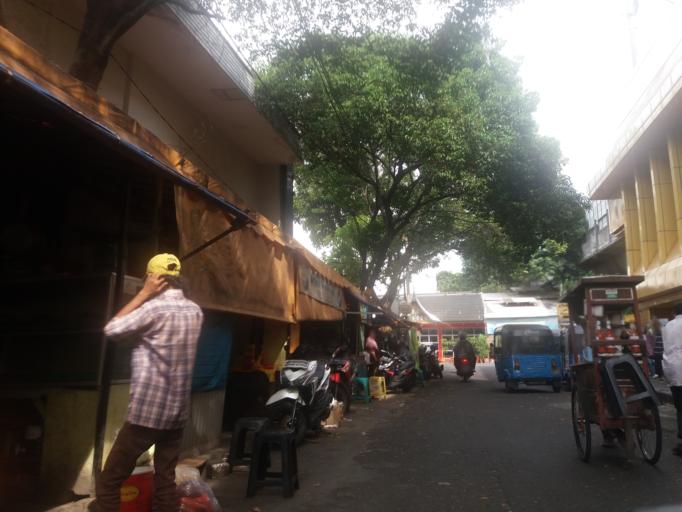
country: ID
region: Jakarta Raya
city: Jakarta
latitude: -6.1866
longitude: 106.8329
